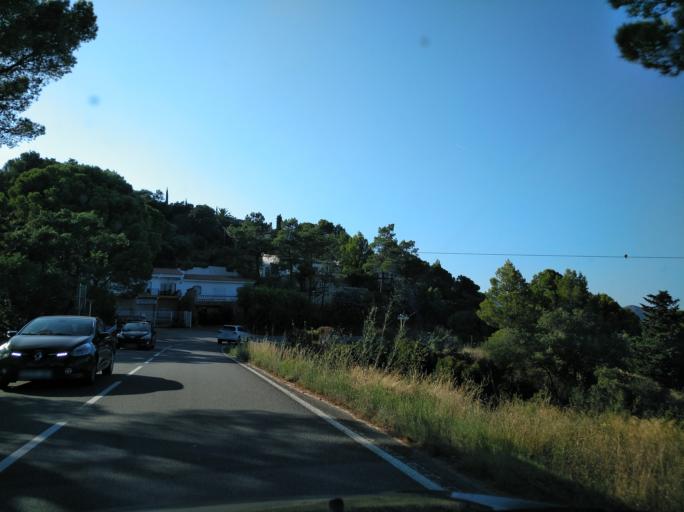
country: ES
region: Catalonia
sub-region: Provincia de Girona
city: Llanca
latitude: 42.3525
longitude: 3.1752
